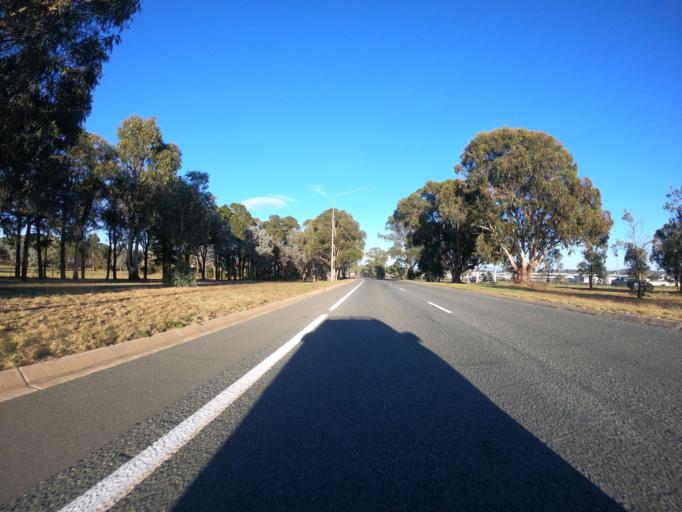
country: AU
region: Australian Capital Territory
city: Kaleen
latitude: -35.2269
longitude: 149.1582
